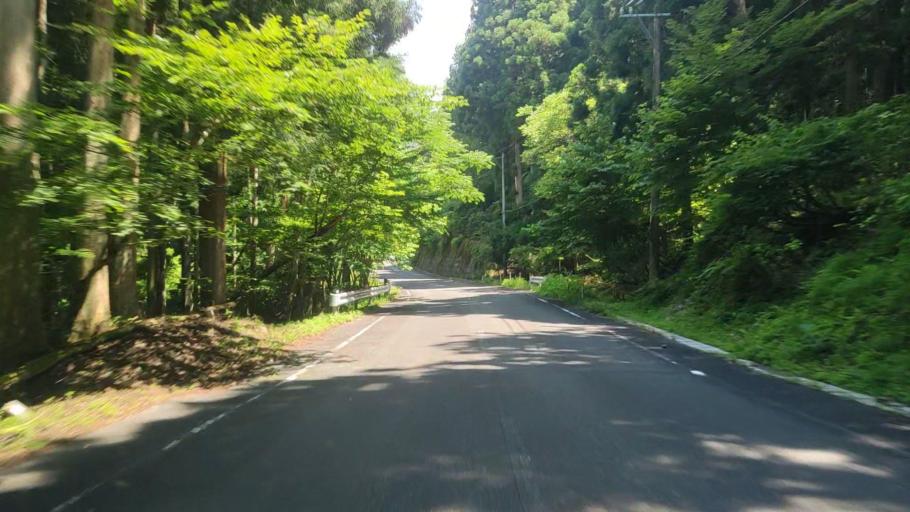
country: JP
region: Fukui
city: Ono
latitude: 35.7221
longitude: 136.5808
